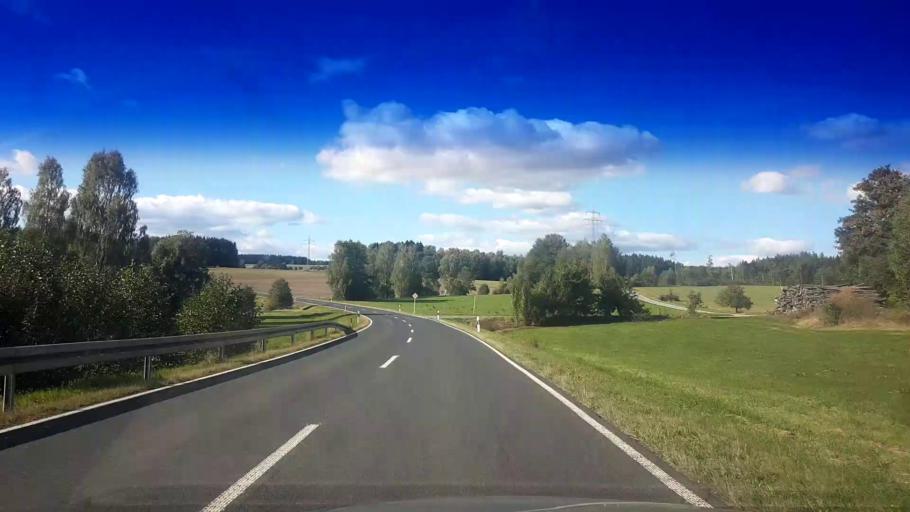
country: DE
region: Bavaria
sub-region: Upper Franconia
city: Marktredwitz
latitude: 50.0363
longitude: 12.0829
